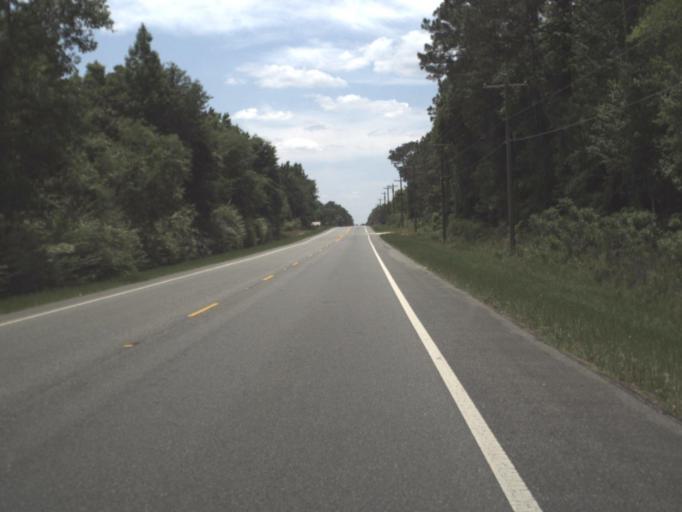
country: US
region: Florida
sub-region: Calhoun County
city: Blountstown
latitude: 30.4230
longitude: -85.0670
